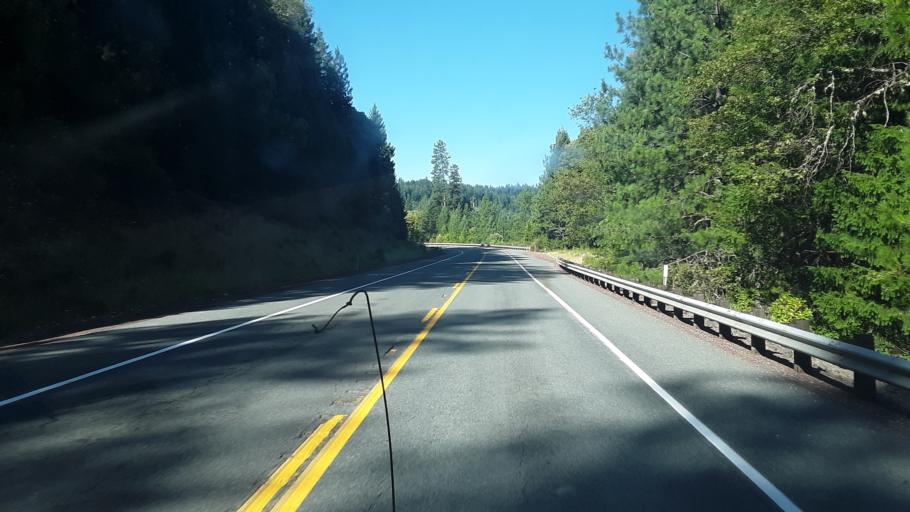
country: US
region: Oregon
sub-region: Jackson County
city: Shady Cove
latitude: 42.6704
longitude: -122.6404
